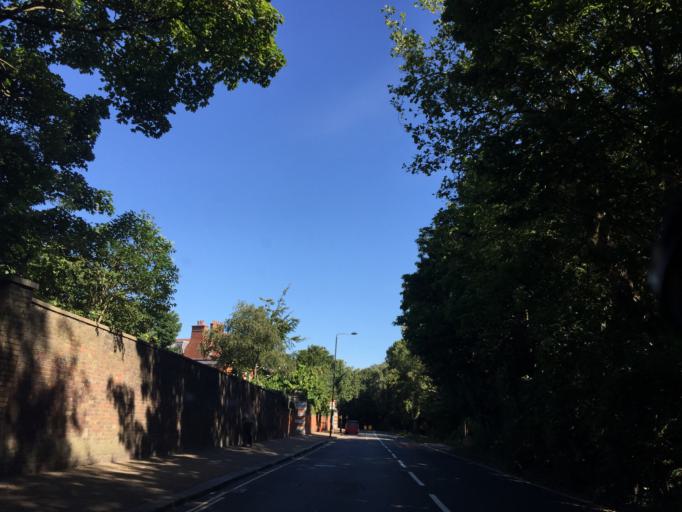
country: GB
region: England
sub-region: Greater London
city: Belsize Park
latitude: 51.5639
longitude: -0.1803
